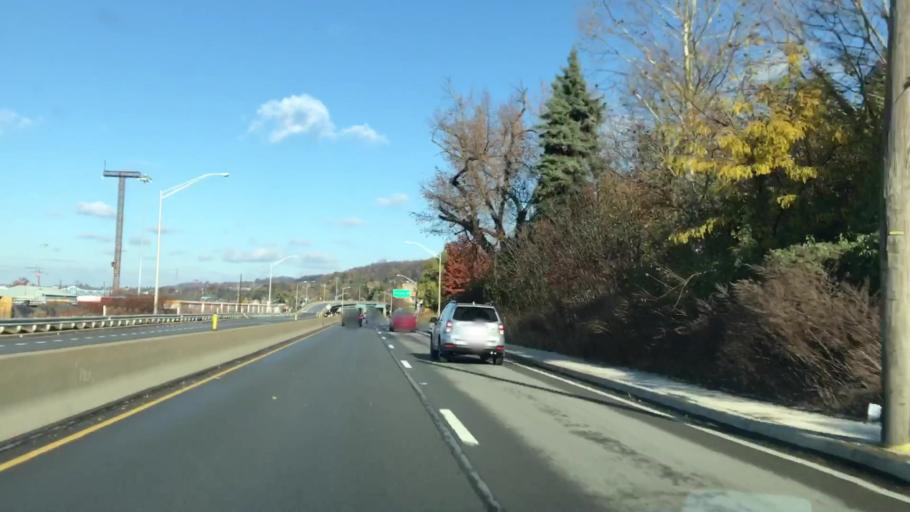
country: US
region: Pennsylvania
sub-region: Beaver County
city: Freedom
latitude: 40.6771
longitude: -80.2481
